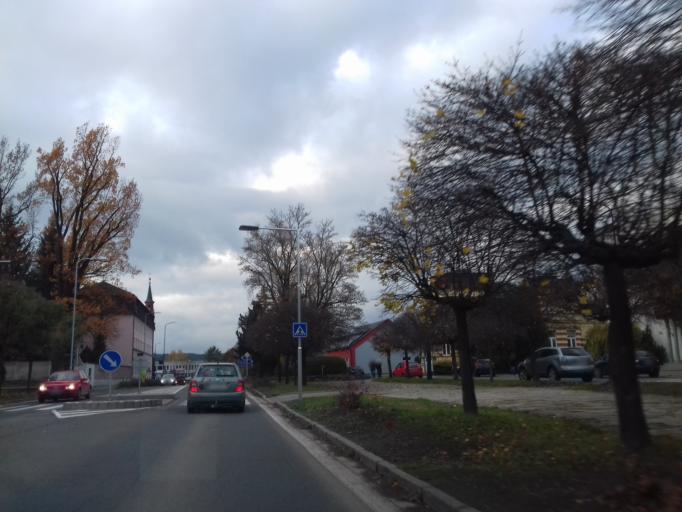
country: CZ
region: Pardubicky
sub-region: Okres Svitavy
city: Svitavy
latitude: 49.7573
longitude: 16.4634
